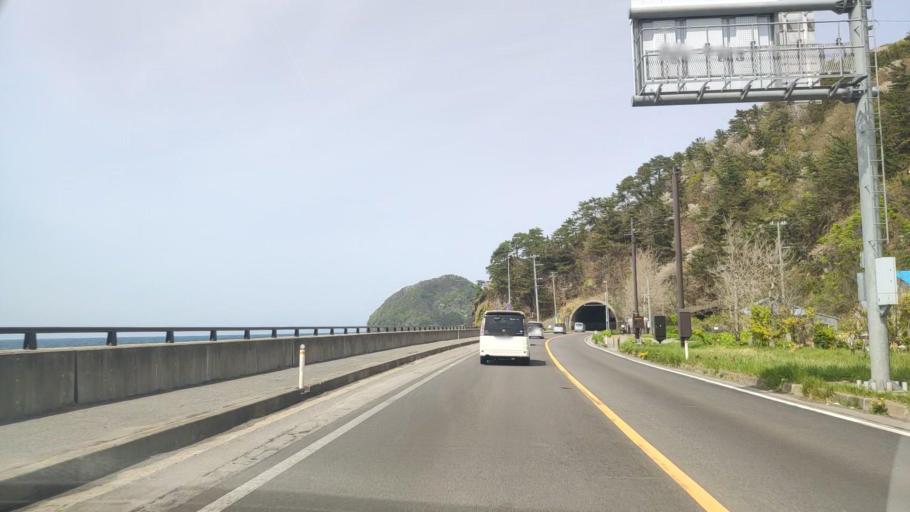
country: JP
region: Aomori
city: Aomori Shi
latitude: 40.8813
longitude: 140.8501
